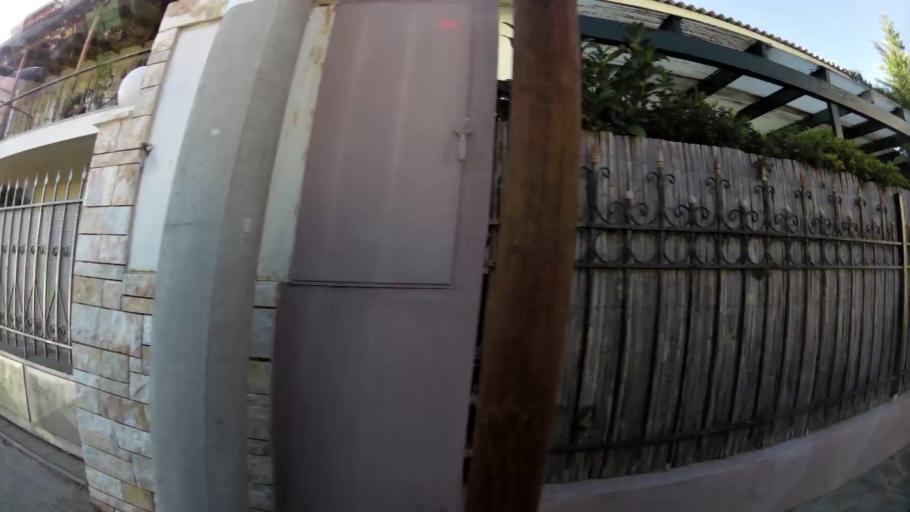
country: GR
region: Attica
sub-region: Nomarchia Anatolikis Attikis
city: Leondarion
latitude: 37.9793
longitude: 23.8448
